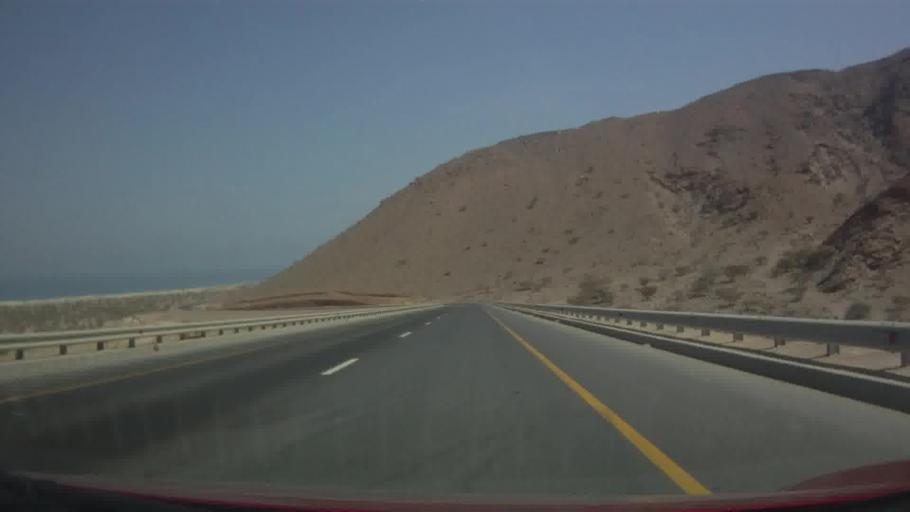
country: OM
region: Muhafazat Masqat
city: Muscat
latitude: 23.3928
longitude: 58.7917
